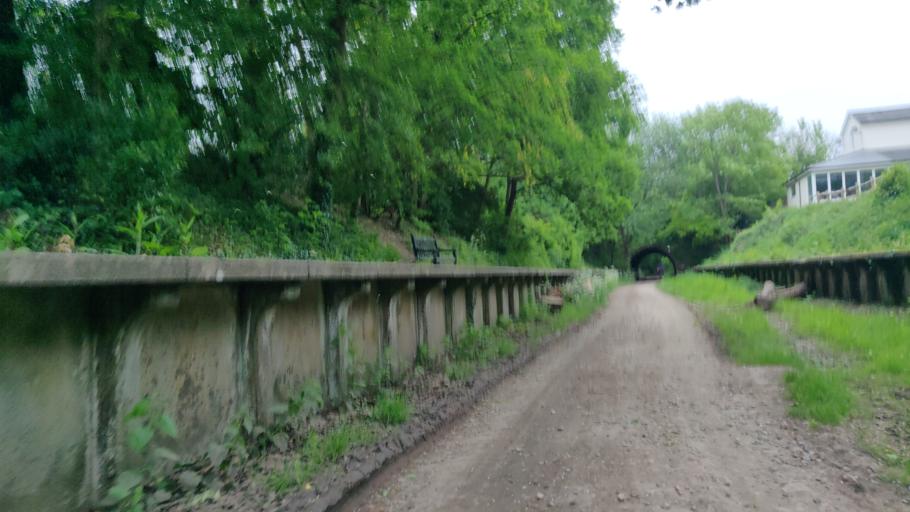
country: GB
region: England
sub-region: West Sussex
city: Partridge Green
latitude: 50.9901
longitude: -0.3143
